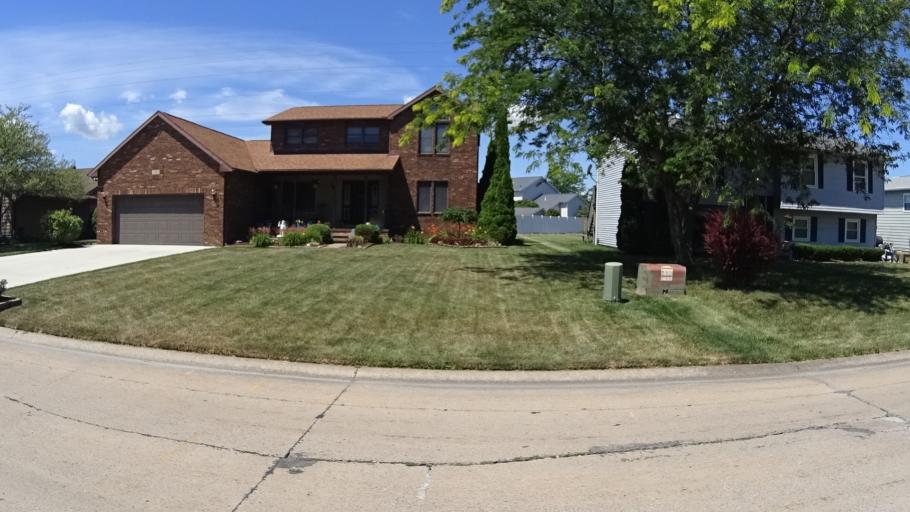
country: US
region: Ohio
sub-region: Erie County
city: Sandusky
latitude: 41.4053
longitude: -82.6925
